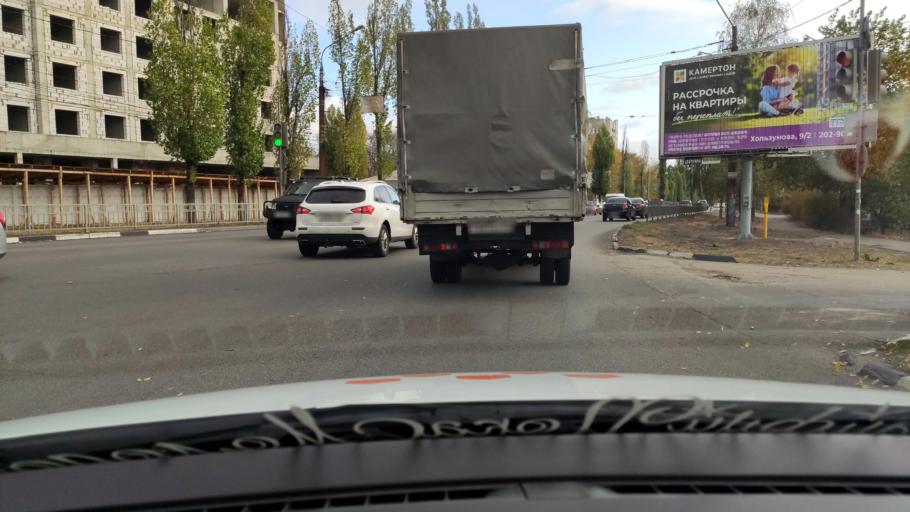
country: RU
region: Voronezj
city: Voronezh
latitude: 51.6958
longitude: 39.1966
